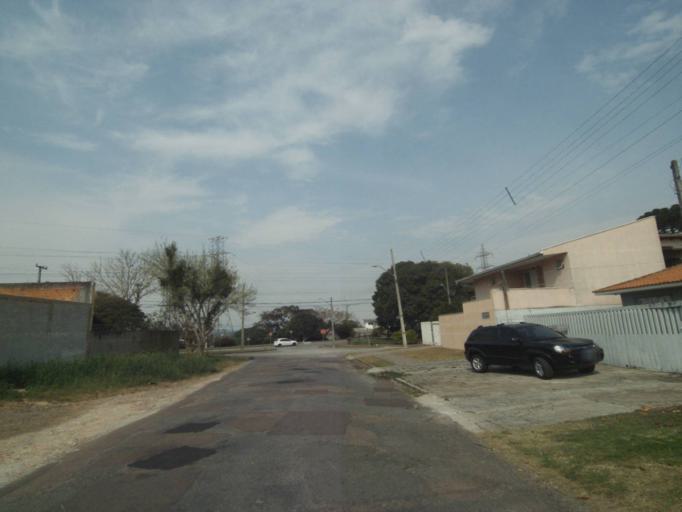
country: BR
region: Parana
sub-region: Pinhais
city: Pinhais
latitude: -25.4813
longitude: -49.2092
